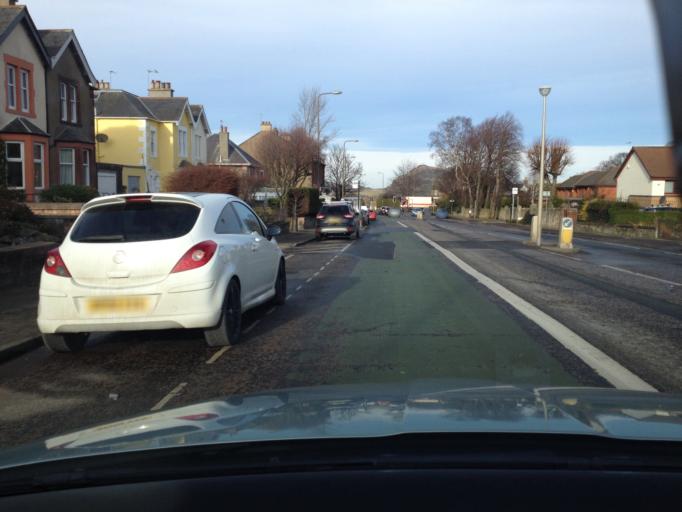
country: GB
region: Scotland
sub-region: Midlothian
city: Loanhead
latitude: 55.9112
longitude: -3.1632
